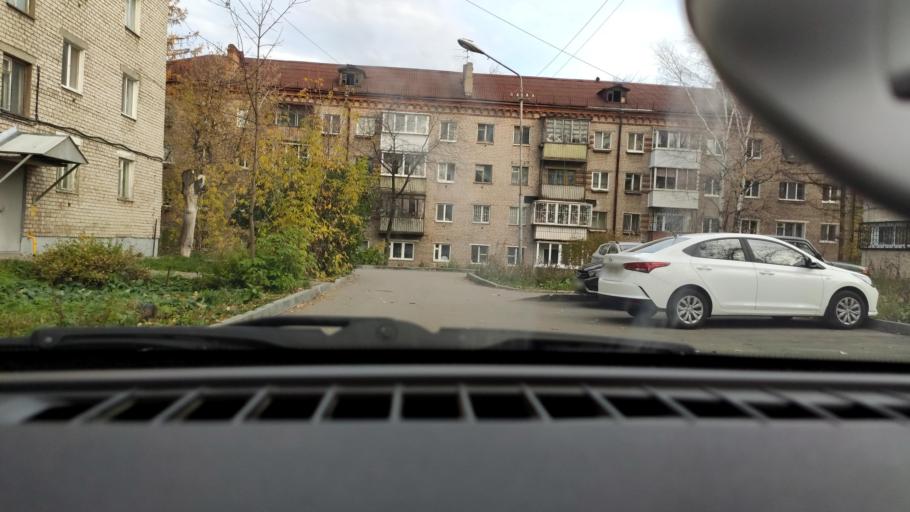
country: RU
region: Perm
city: Froly
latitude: 57.9751
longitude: 56.3181
